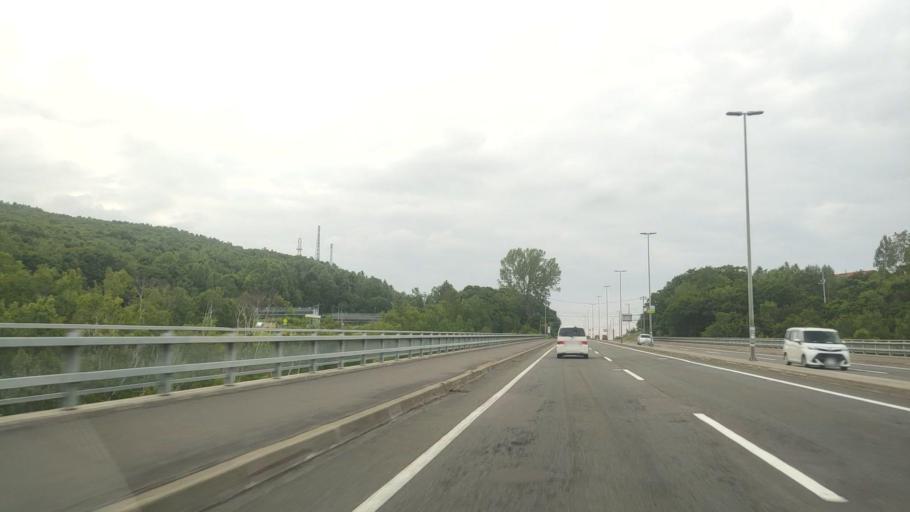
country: JP
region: Hokkaido
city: Otaru
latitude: 43.1587
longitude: 141.1113
